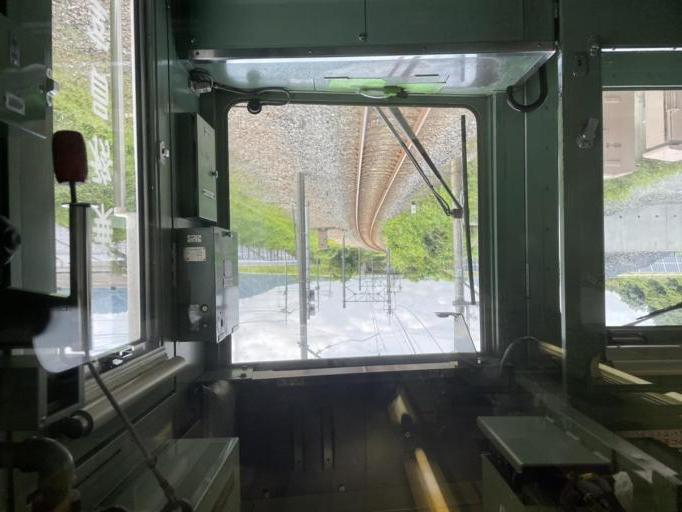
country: JP
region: Tochigi
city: Tanuma
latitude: 36.3872
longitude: 139.6010
